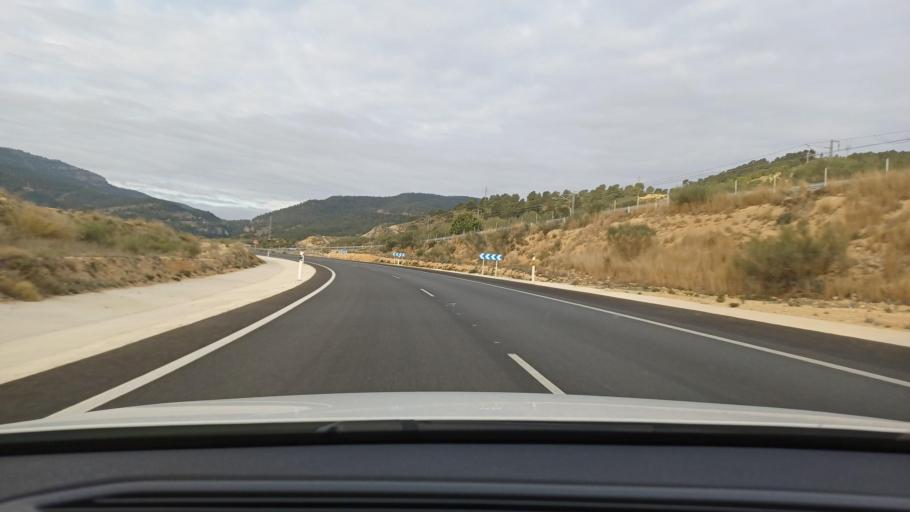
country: ES
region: Valencia
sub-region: Provincia de Valencia
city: La Font de la Figuera
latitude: 38.8307
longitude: -0.8881
